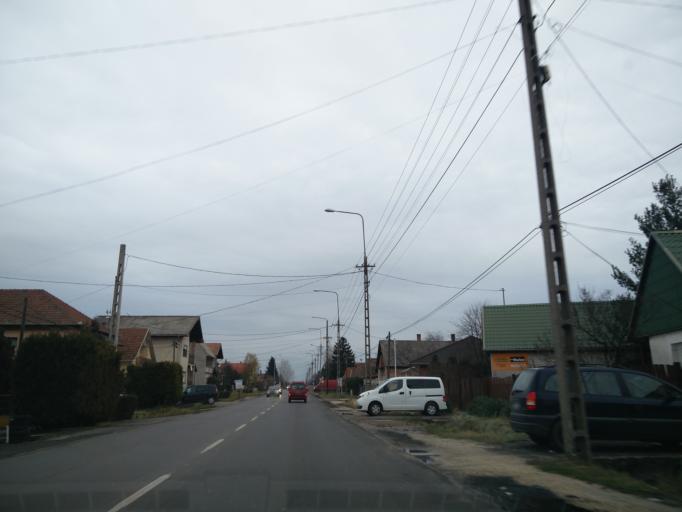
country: HU
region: Pest
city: Ullo
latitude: 47.3897
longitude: 19.3258
